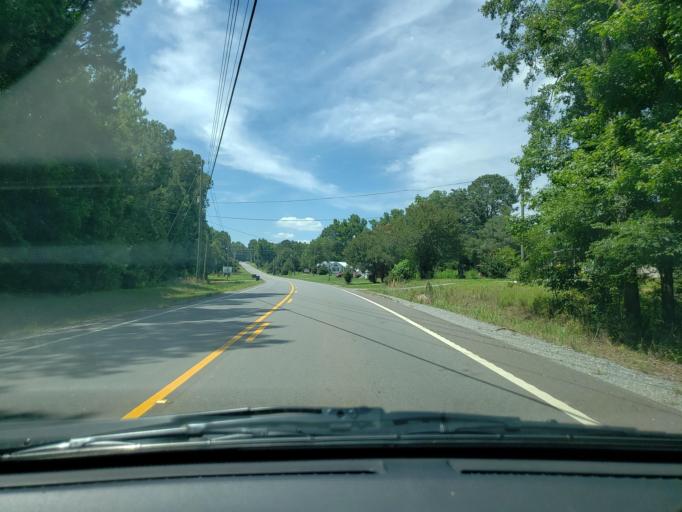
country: US
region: Alabama
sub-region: Elmore County
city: Eclectic
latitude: 32.6689
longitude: -85.9425
